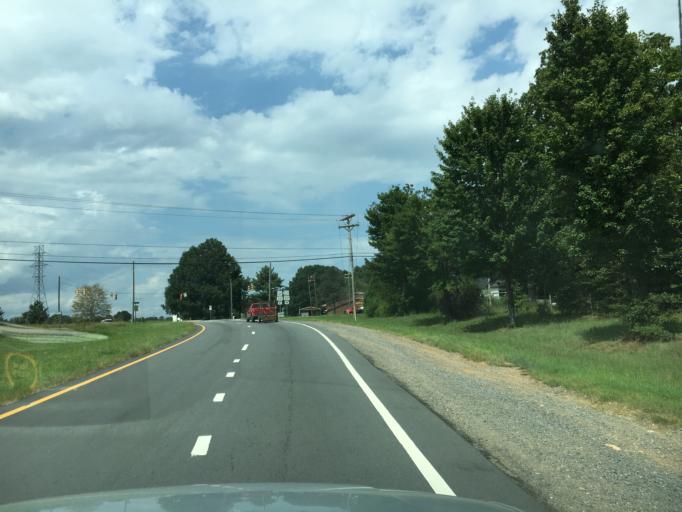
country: US
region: North Carolina
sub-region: Catawba County
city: Maiden
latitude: 35.5277
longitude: -81.2216
